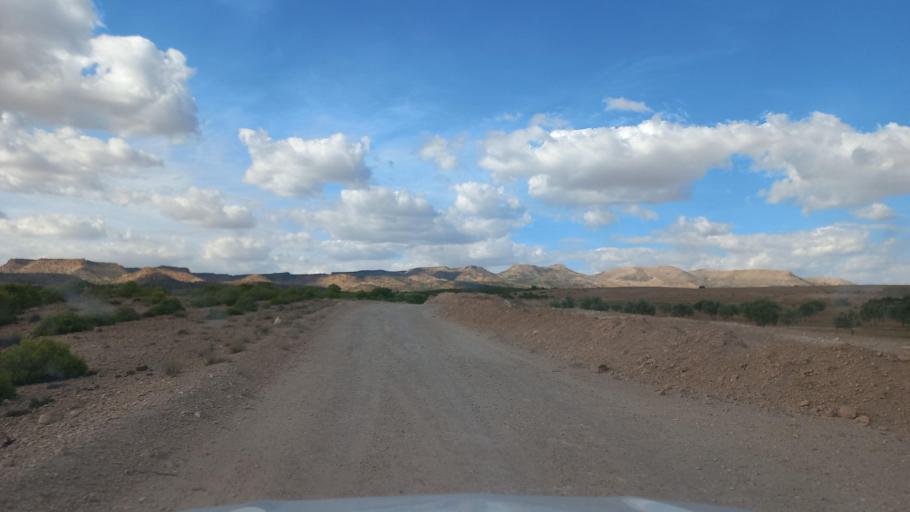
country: TN
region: Al Qasrayn
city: Sbiba
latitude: 35.3997
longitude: 9.0110
